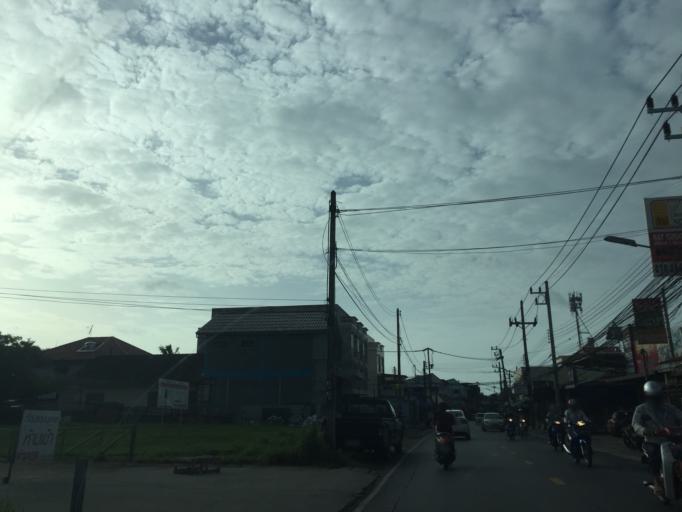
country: TH
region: Phuket
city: Mueang Phuket
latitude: 7.8610
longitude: 98.3743
